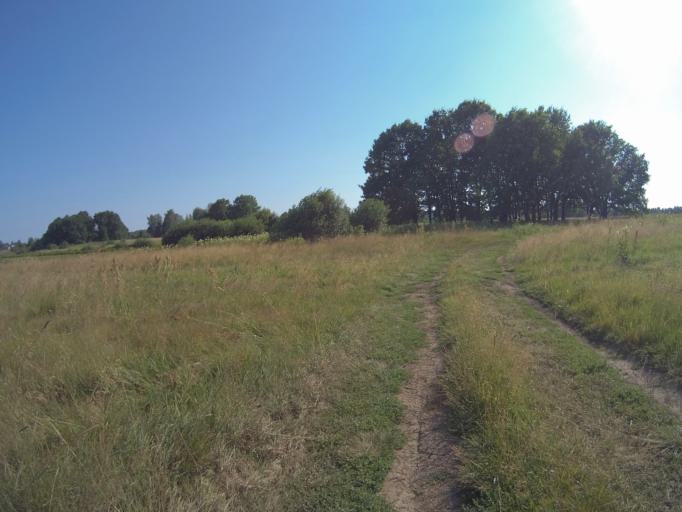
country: RU
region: Vladimir
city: Vorsha
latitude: 56.0285
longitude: 40.2046
